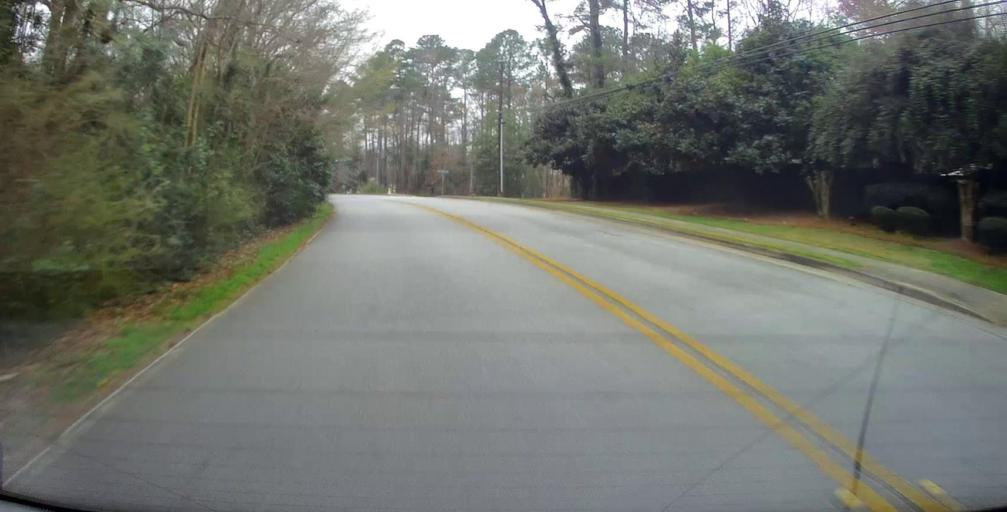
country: US
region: Georgia
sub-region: Bibb County
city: Macon
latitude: 32.9037
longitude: -83.7285
